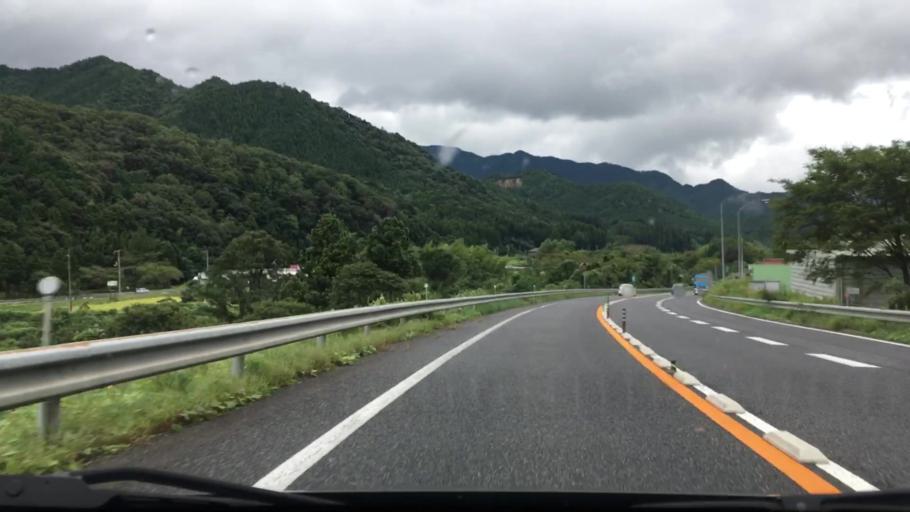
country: JP
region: Hyogo
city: Nishiwaki
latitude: 35.0917
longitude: 134.7768
